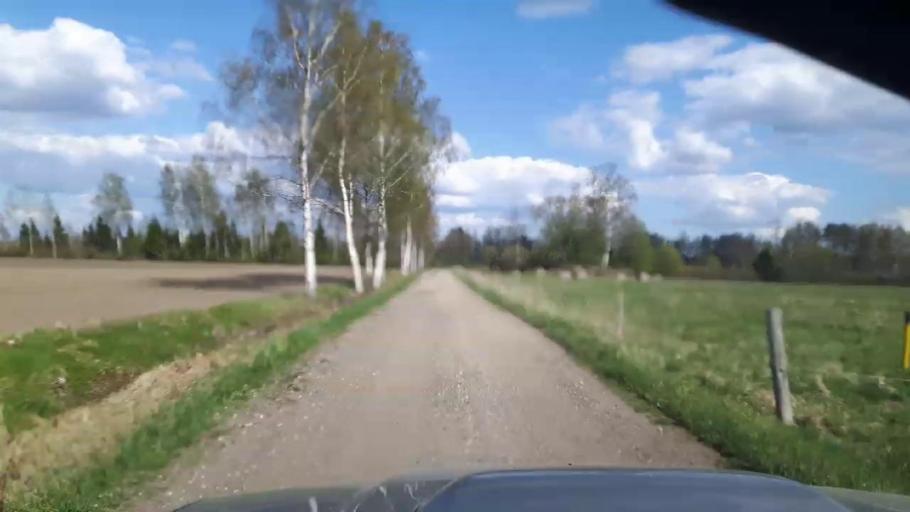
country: EE
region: Paernumaa
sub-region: Tootsi vald
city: Tootsi
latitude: 58.4497
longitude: 24.8546
